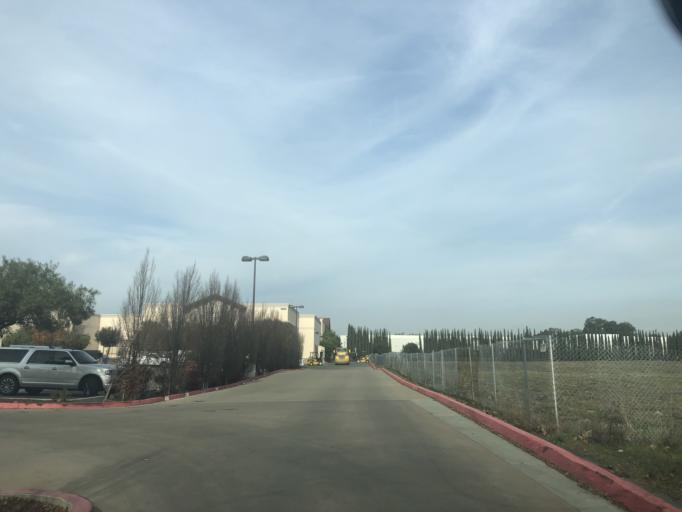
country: US
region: California
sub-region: Contra Costa County
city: Concord
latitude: 38.0043
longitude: -122.0422
